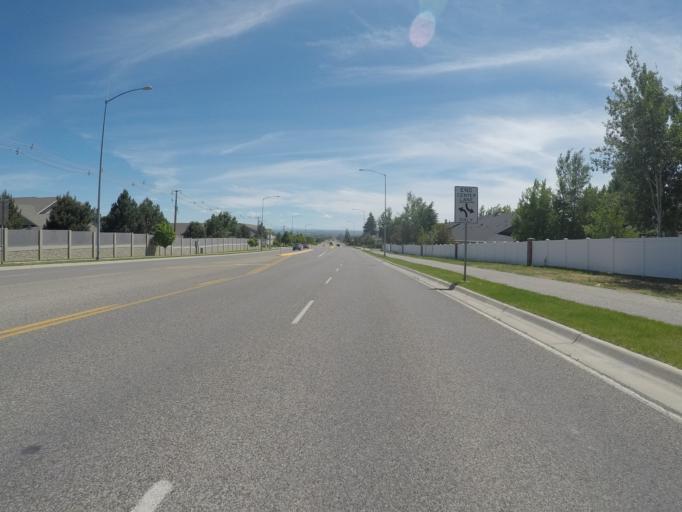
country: US
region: Montana
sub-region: Yellowstone County
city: Billings
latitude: 45.7919
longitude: -108.6177
